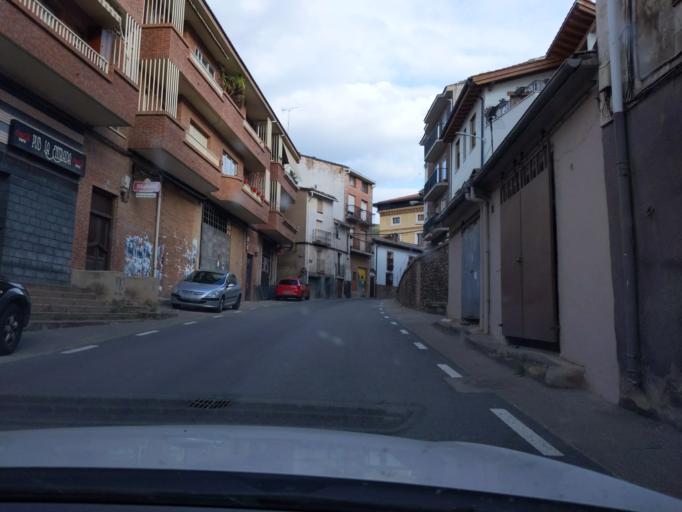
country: ES
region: La Rioja
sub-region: Provincia de La Rioja
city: Nalda
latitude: 42.3357
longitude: -2.4870
